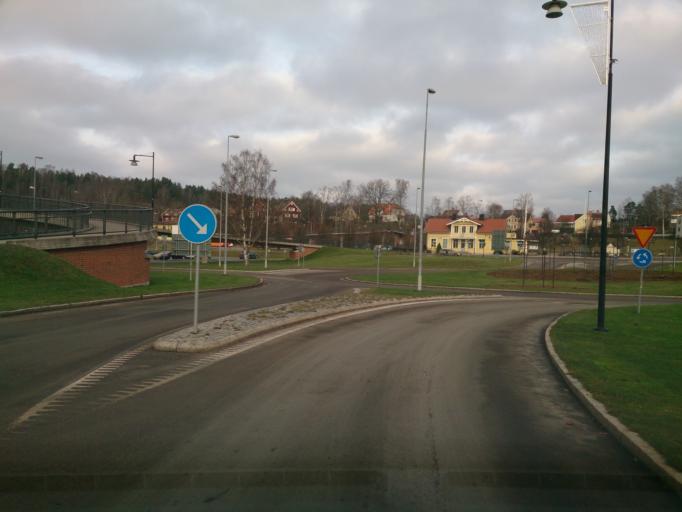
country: SE
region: OEstergoetland
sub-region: Atvidabergs Kommun
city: Atvidaberg
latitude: 58.2021
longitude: 16.0009
